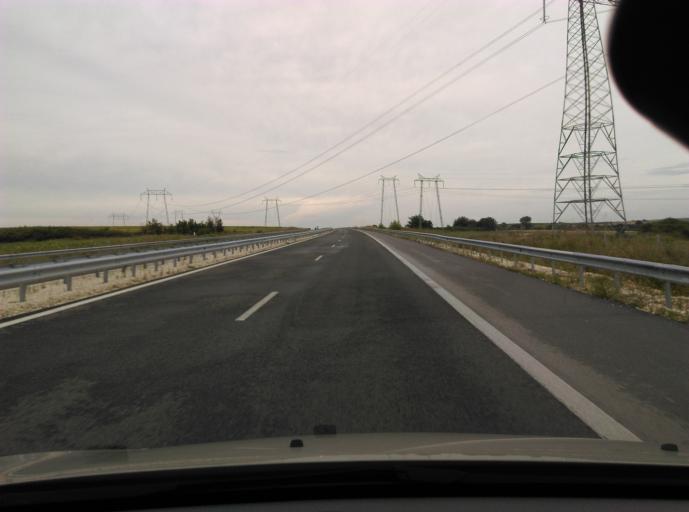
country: BG
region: Stara Zagora
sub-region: Obshtina Chirpan
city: Chirpan
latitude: 42.1279
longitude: 25.3657
